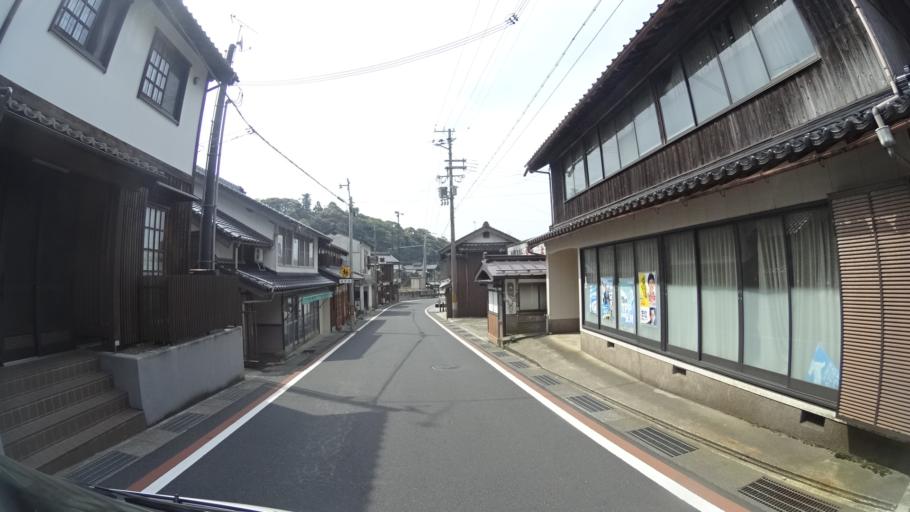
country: JP
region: Kyoto
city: Miyazu
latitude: 35.6765
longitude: 135.2872
